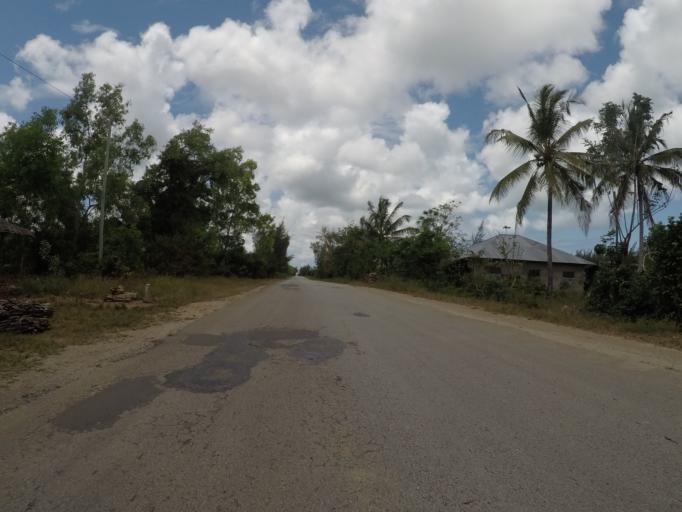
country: TZ
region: Zanzibar Central/South
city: Mahonda
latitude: -6.3146
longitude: 39.4322
